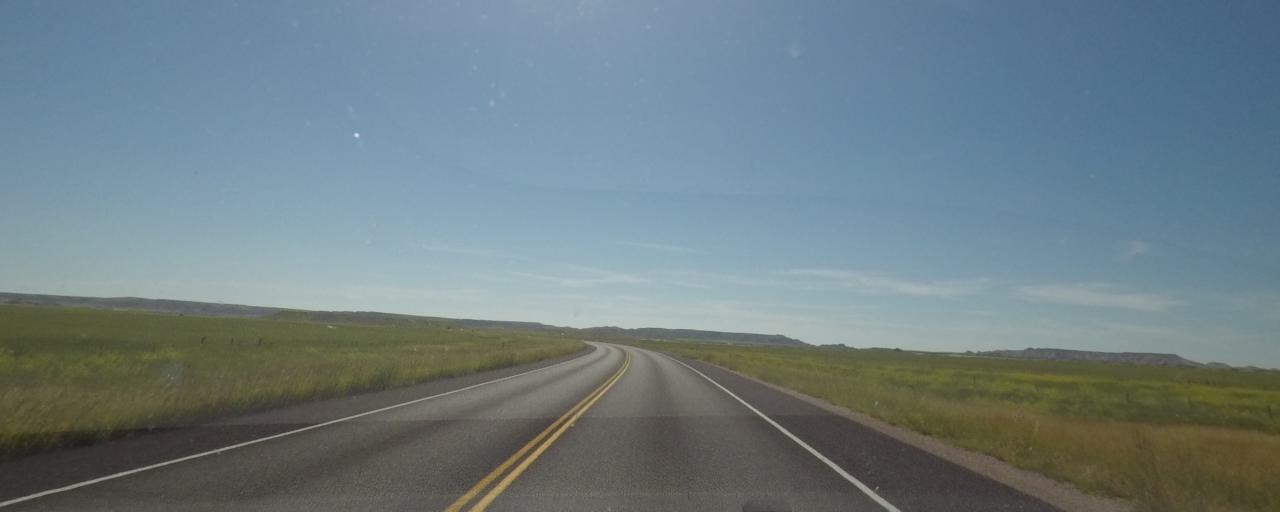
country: US
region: South Dakota
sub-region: Shannon County
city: Porcupine
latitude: 43.7795
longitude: -102.5478
